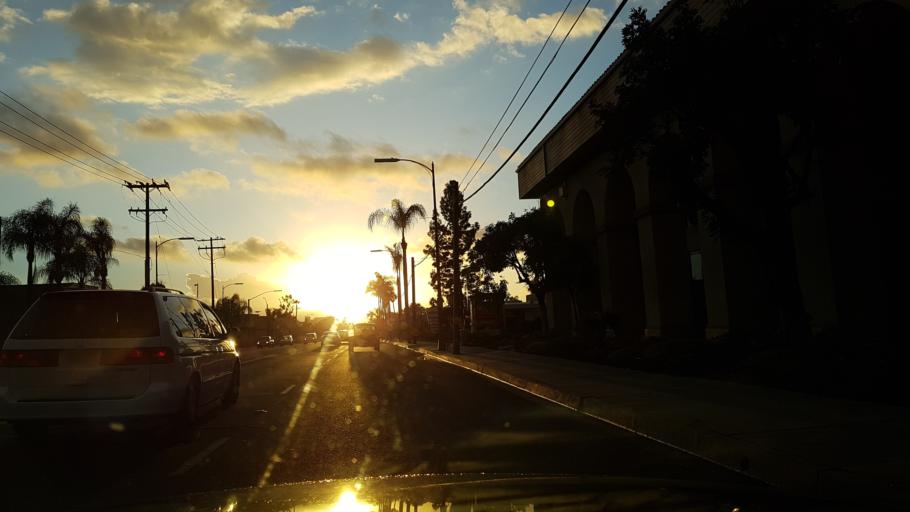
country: US
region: California
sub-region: San Diego County
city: Escondido
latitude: 33.1337
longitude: -117.0602
